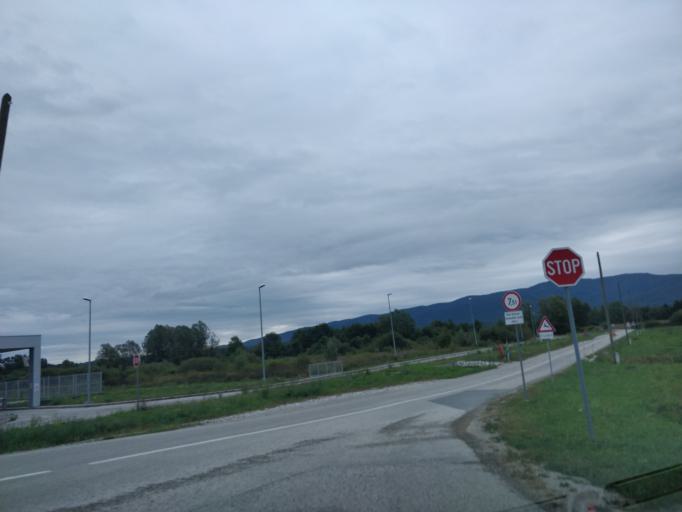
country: HR
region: Zagrebacka
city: Jakovlje
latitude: 45.9561
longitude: 15.8295
